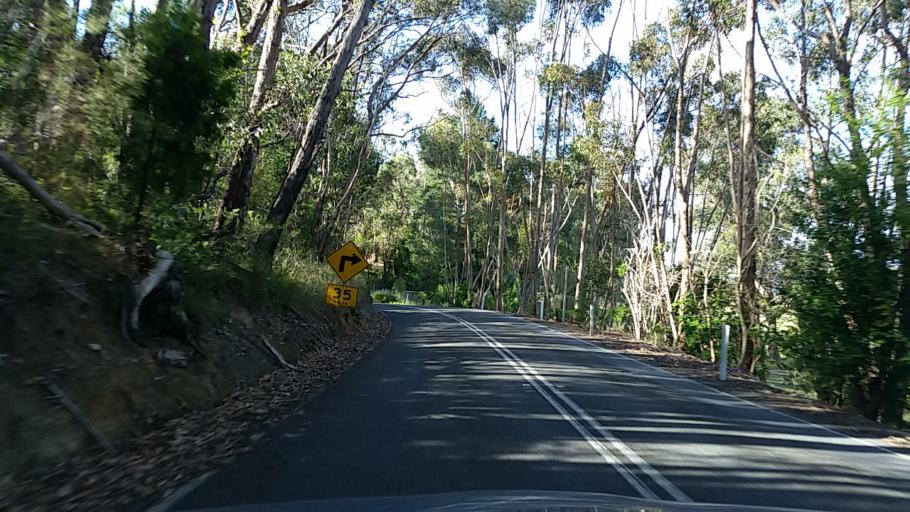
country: AU
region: South Australia
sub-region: Adelaide Hills
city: Stirling
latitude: -35.0337
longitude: 138.7648
